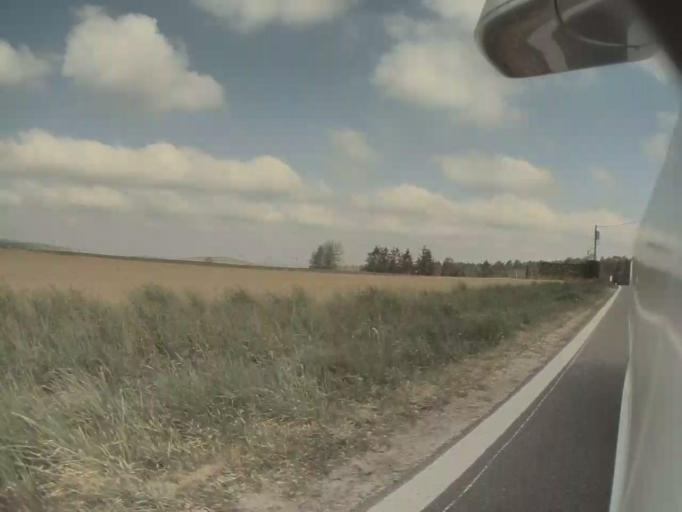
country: BE
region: Wallonia
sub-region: Province du Luxembourg
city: Tellin
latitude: 50.0939
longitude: 5.2323
